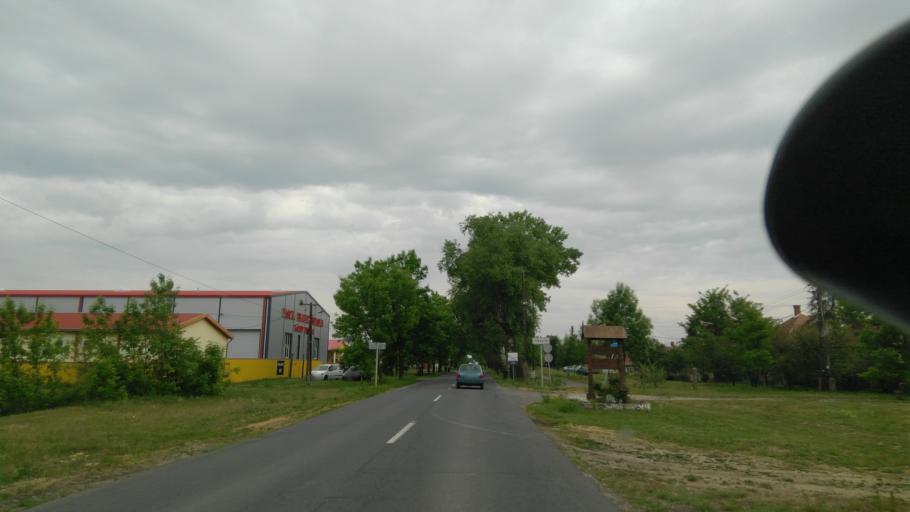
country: HU
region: Bekes
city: Veszto
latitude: 46.9003
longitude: 21.2518
